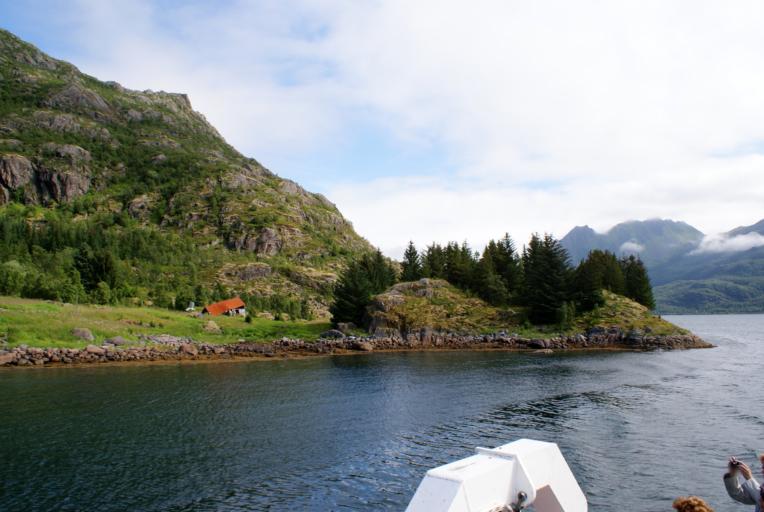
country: NO
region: Nordland
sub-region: Hadsel
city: Stokmarknes
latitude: 68.3676
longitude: 15.0292
